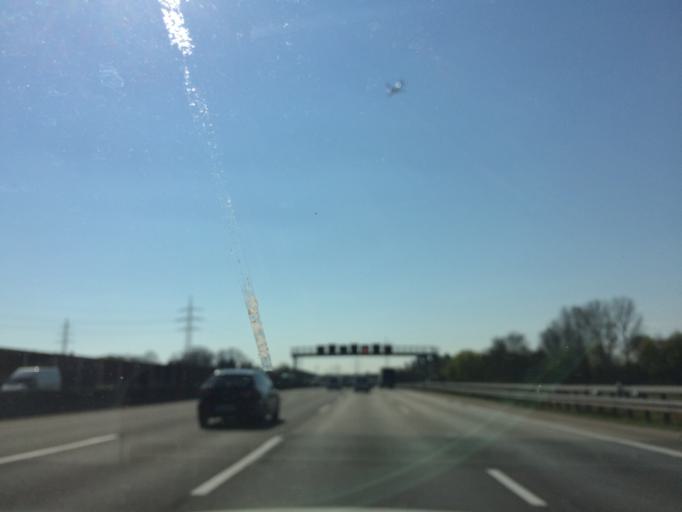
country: DE
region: North Rhine-Westphalia
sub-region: Regierungsbezirk Koln
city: Merheim
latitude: 50.9517
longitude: 7.0371
